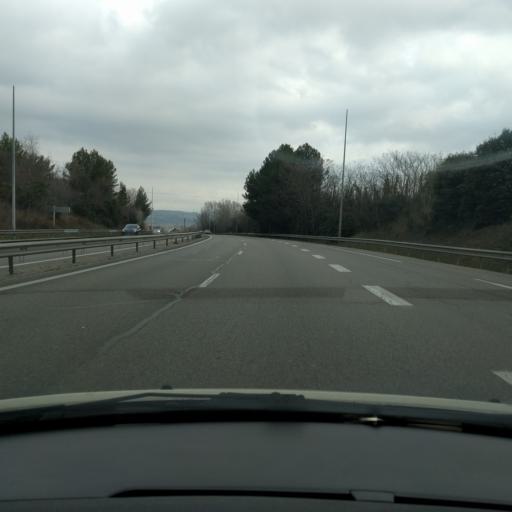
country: FR
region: Provence-Alpes-Cote d'Azur
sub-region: Departement des Bouches-du-Rhone
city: Gardanne
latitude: 43.4507
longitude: 5.4511
